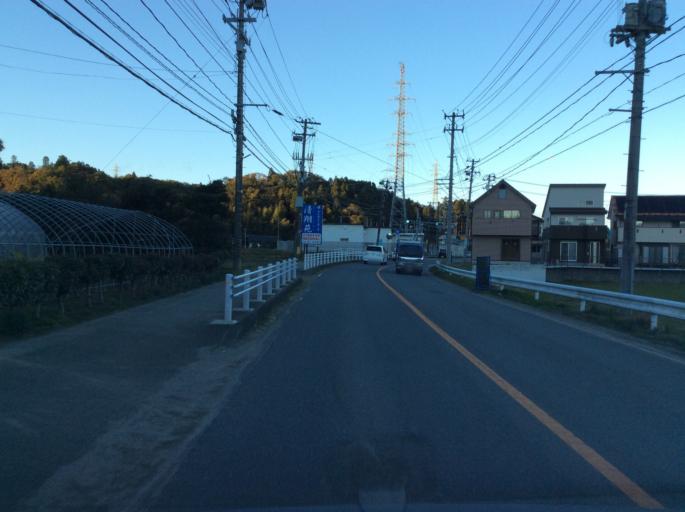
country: JP
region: Fukushima
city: Iwaki
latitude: 37.0650
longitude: 140.8701
